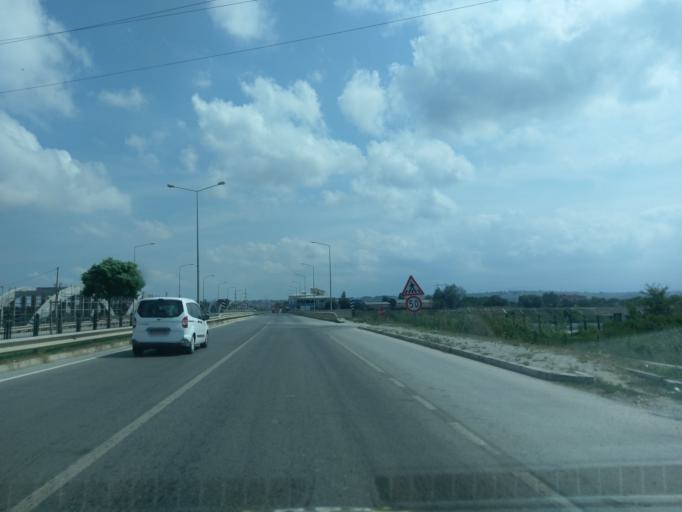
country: TR
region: Samsun
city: Bafra
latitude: 41.5680
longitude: 35.8792
